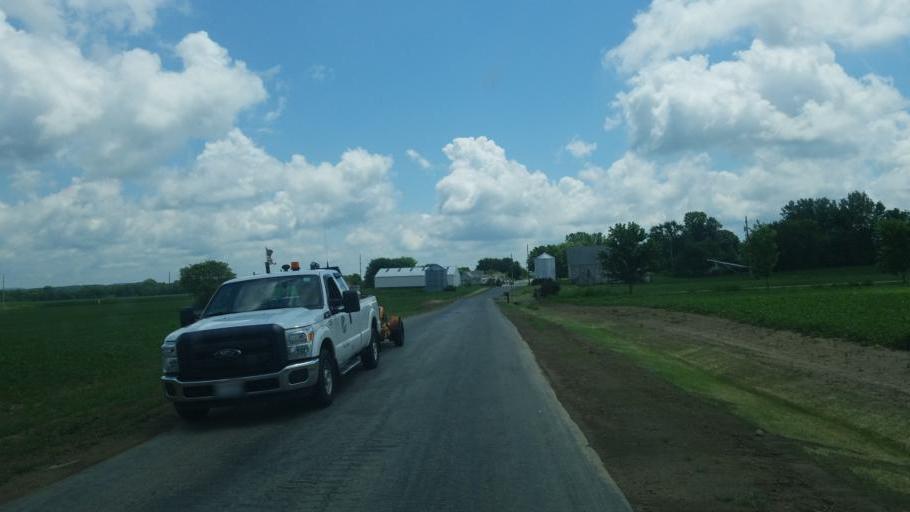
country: US
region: Ohio
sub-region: Highland County
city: Greenfield
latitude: 39.2646
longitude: -83.4474
